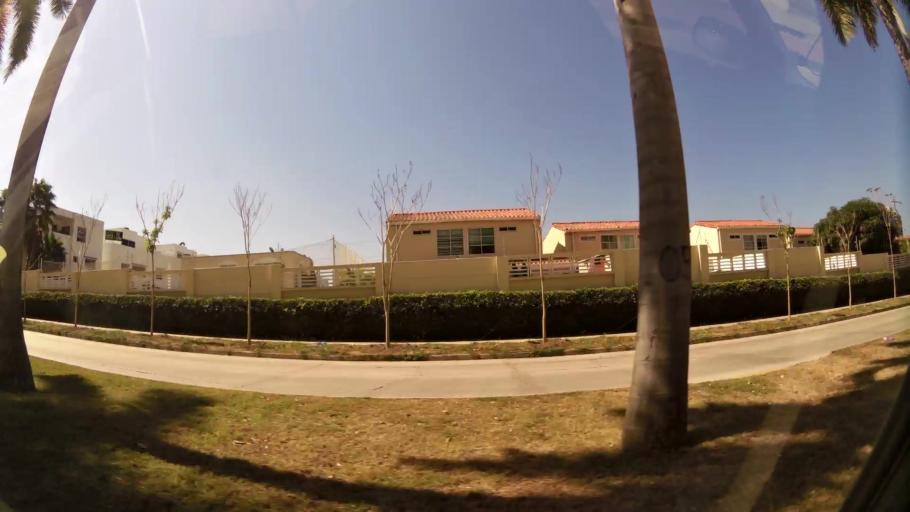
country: CO
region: Atlantico
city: Barranquilla
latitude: 11.0168
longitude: -74.8335
